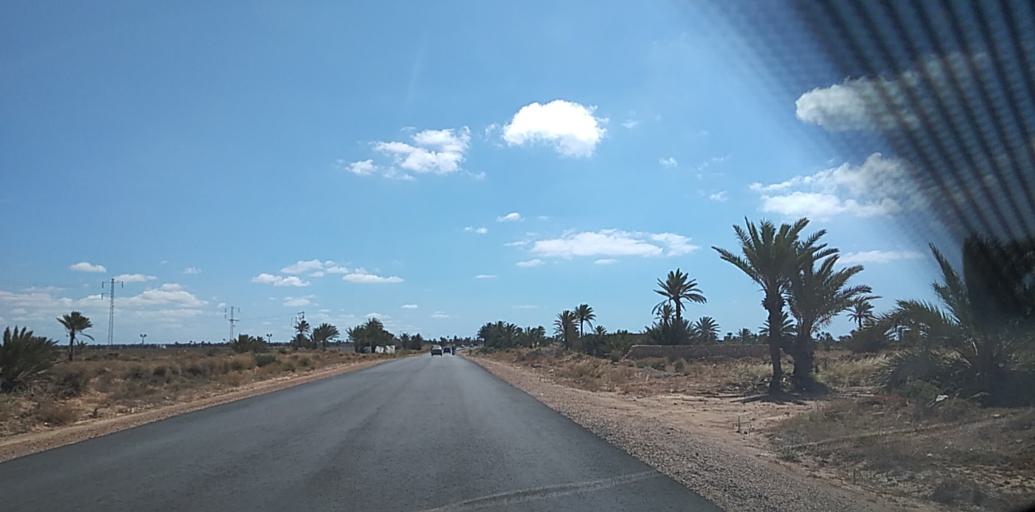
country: TN
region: Safaqis
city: Al Qarmadah
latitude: 34.6581
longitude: 11.1013
